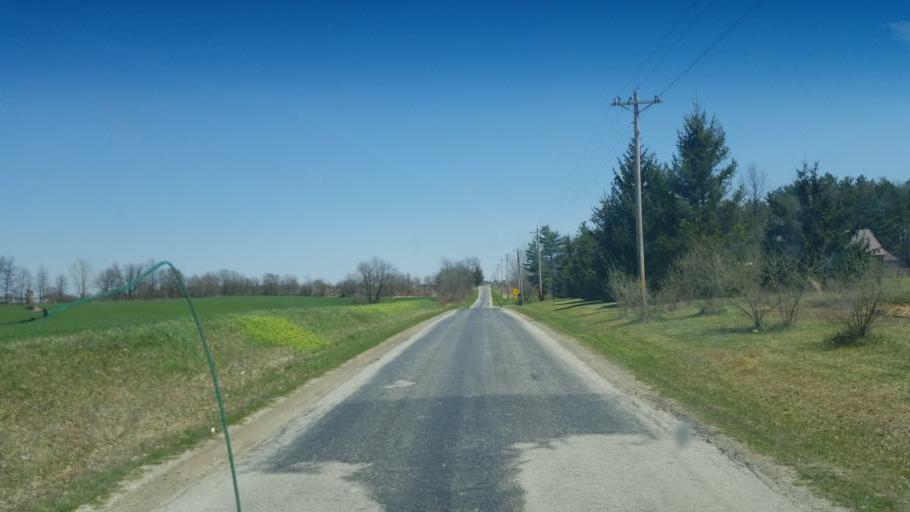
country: US
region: Ohio
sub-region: Huron County
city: Greenwich
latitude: 41.0478
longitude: -82.4983
